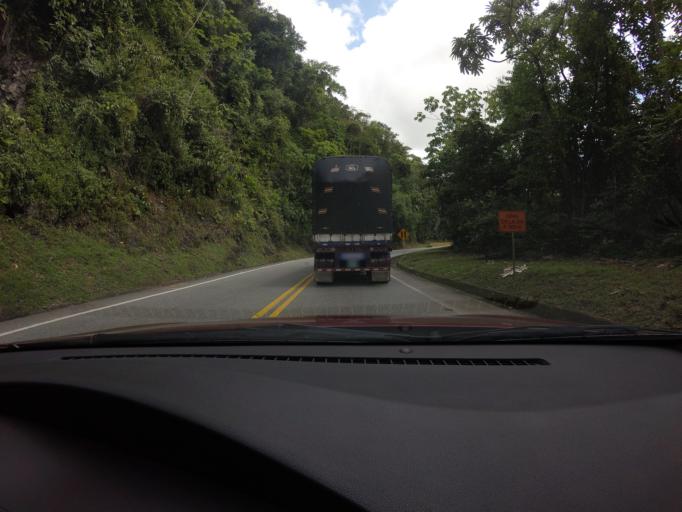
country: CO
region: Antioquia
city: San Luis
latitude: 5.9919
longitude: -74.9351
